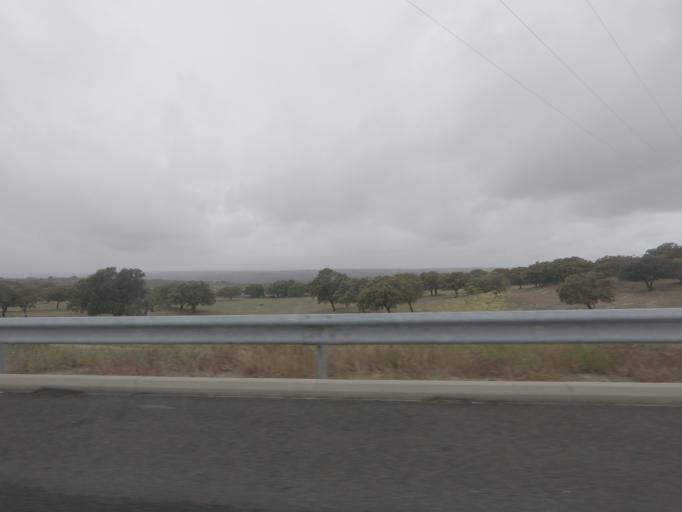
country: ES
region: Extremadura
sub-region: Provincia de Caceres
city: Santiago del Campo
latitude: 39.6394
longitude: -6.3940
